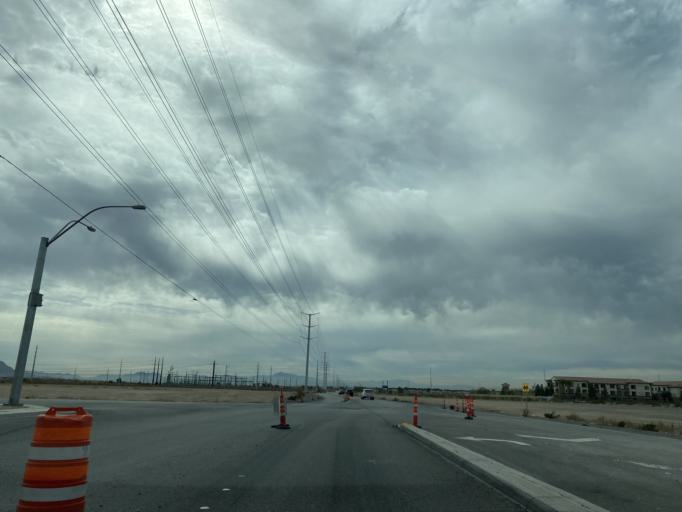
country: US
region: Nevada
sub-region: Clark County
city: Nellis Air Force Base
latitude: 36.2827
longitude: -115.0987
